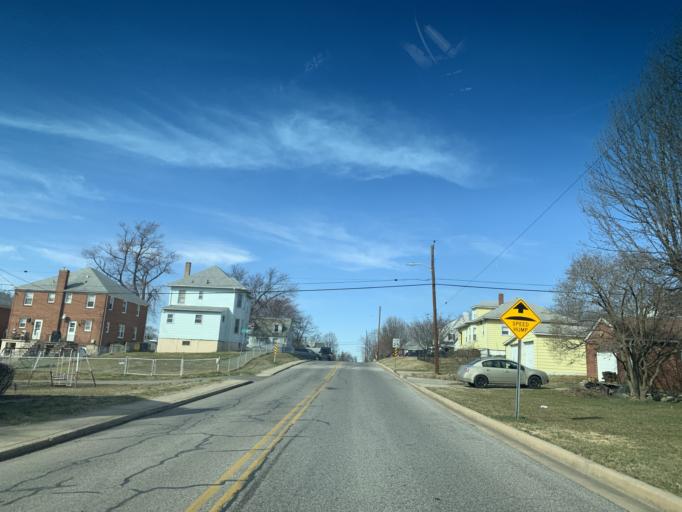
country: US
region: Maryland
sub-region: Anne Arundel County
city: Brooklyn Park
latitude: 39.2260
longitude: -76.6150
